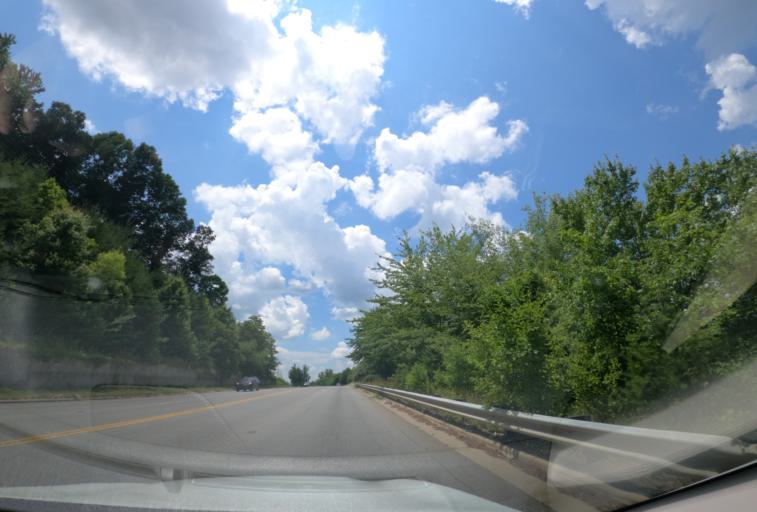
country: US
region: North Carolina
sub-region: Haywood County
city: Lake Junaluska
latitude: 35.5209
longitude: -82.9607
